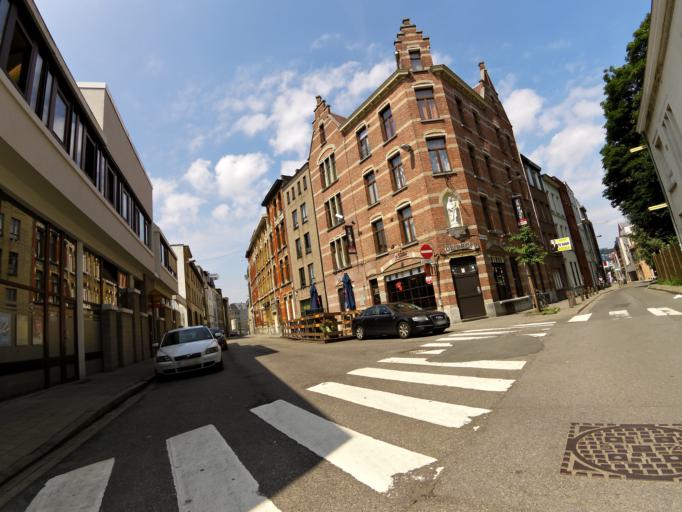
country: BE
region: Flanders
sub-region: Provincie Antwerpen
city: Antwerpen
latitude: 51.2234
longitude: 4.4116
